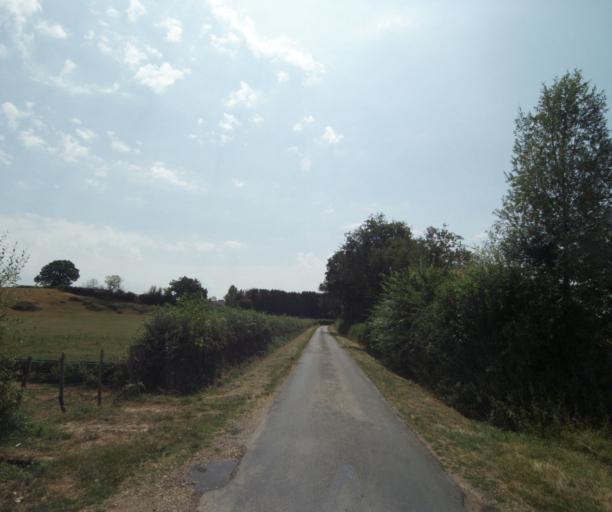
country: FR
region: Bourgogne
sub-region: Departement de Saone-et-Loire
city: Gueugnon
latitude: 46.5687
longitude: 4.0595
